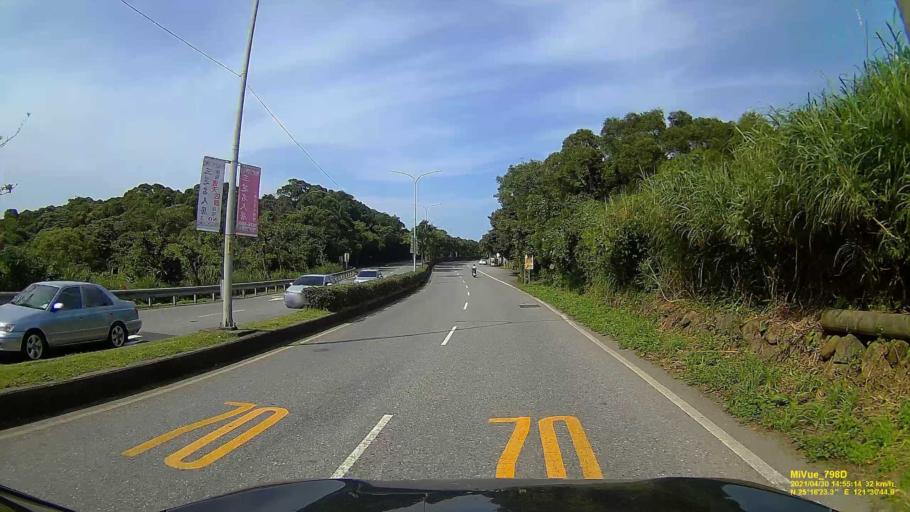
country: TW
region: Taipei
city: Taipei
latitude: 25.2733
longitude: 121.5127
